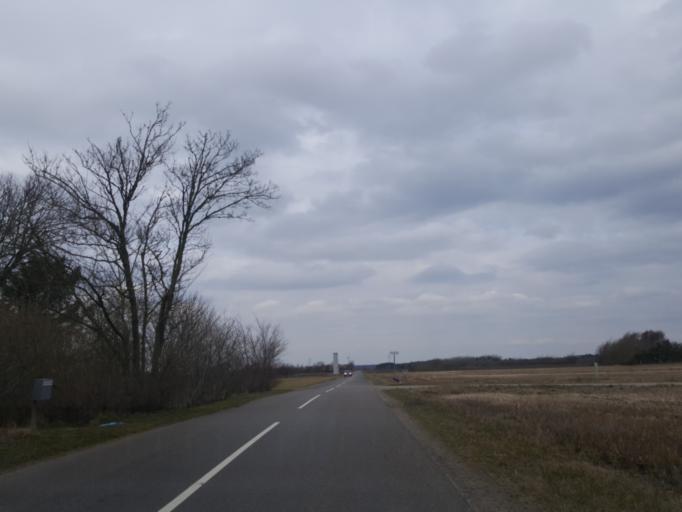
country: DK
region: Central Jutland
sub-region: Lemvig Kommune
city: Lemvig
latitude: 56.4178
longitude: 8.2328
